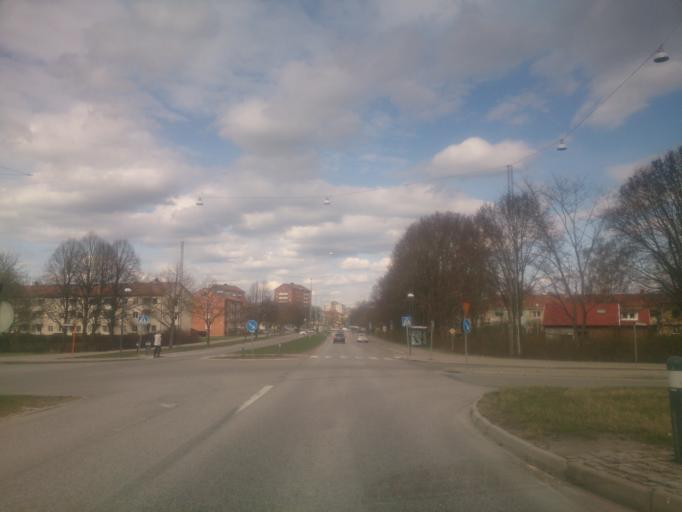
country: SE
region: OEstergoetland
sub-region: Norrkopings Kommun
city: Norrkoping
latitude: 58.5771
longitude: 16.1808
